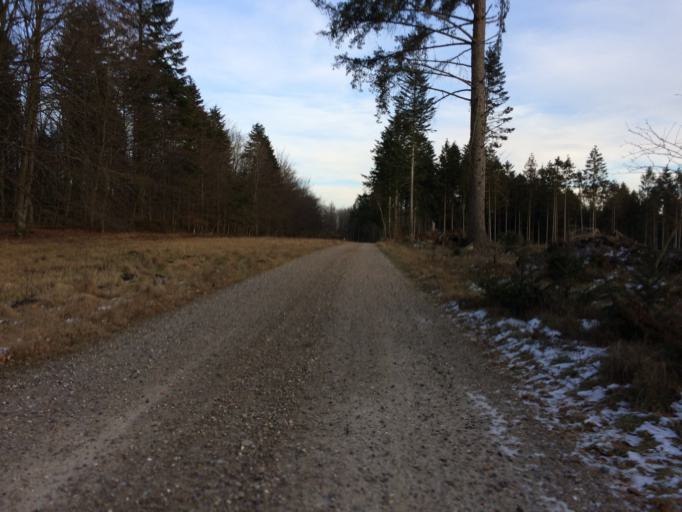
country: DK
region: Central Jutland
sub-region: Holstebro Kommune
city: Ulfborg
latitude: 56.2543
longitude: 8.4679
